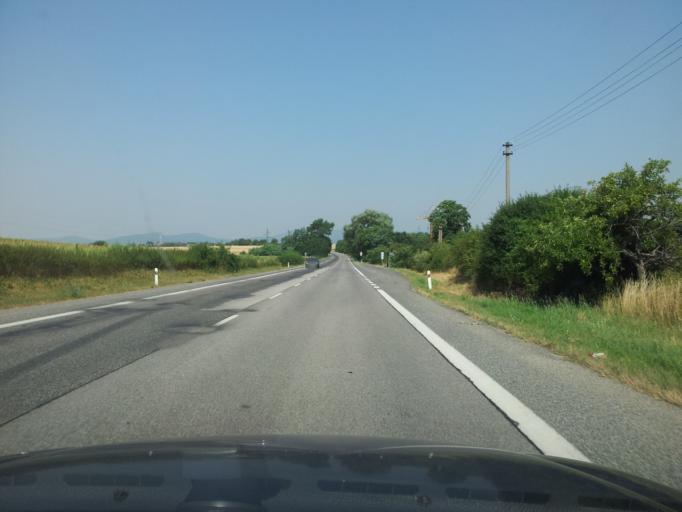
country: SK
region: Nitriansky
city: Zlate Moravce
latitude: 48.3678
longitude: 18.4433
